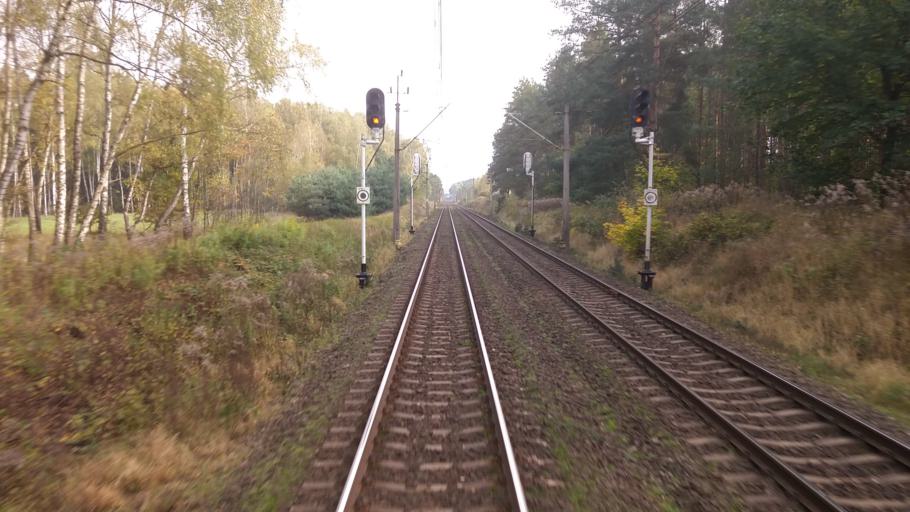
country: PL
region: West Pomeranian Voivodeship
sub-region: Powiat choszczenski
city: Choszczno
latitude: 53.1654
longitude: 15.3620
